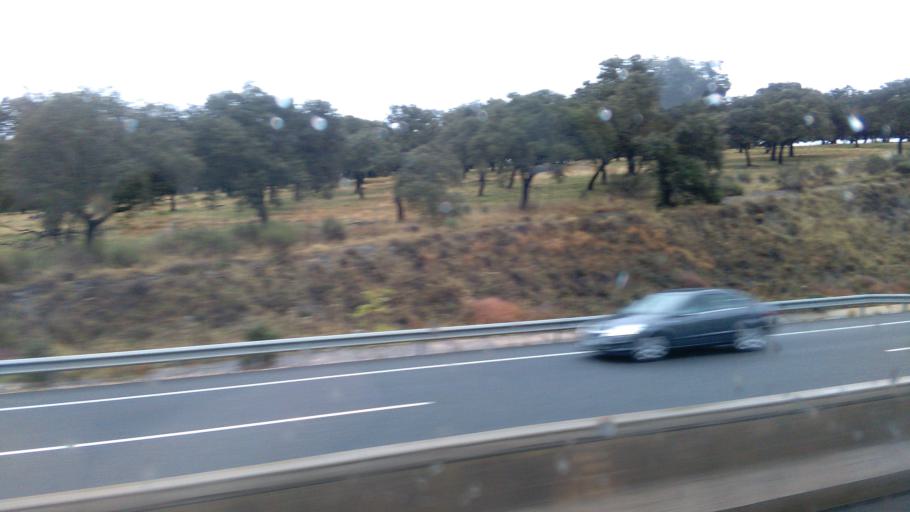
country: ES
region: Extremadura
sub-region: Provincia de Caceres
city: Casas de Miravete
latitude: 39.7578
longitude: -5.7321
